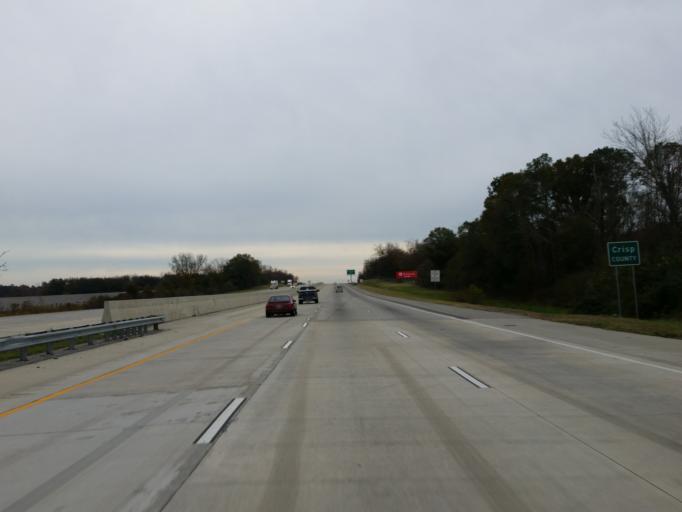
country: US
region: Georgia
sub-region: Crisp County
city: Cordele
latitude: 32.0297
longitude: -83.7627
